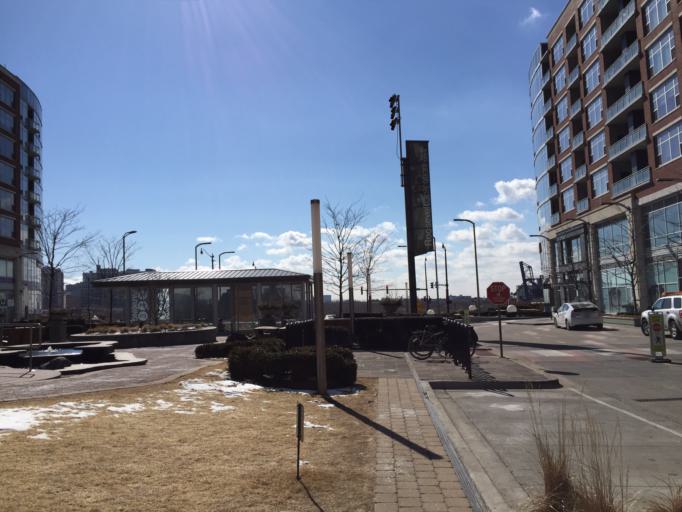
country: US
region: Illinois
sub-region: Cook County
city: Chicago
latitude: 41.8683
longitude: -87.6326
